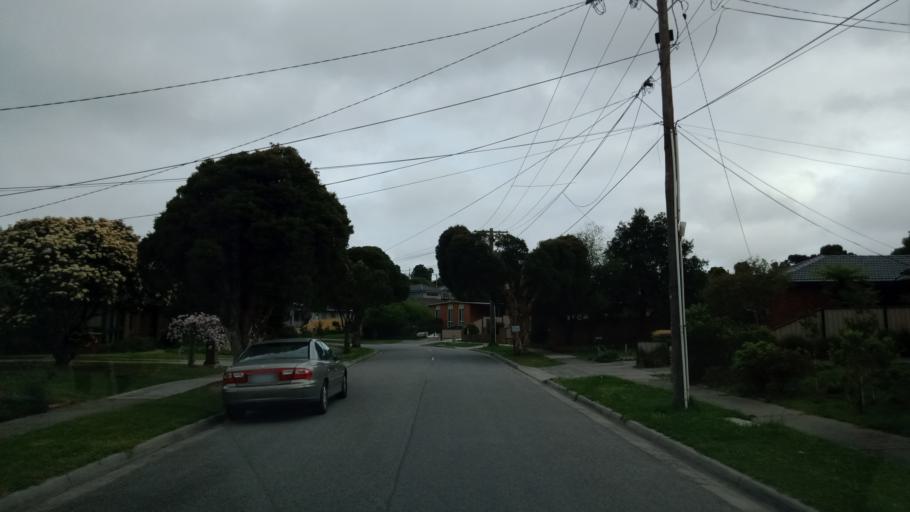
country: AU
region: Victoria
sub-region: Casey
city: Eumemmerring
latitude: -37.9907
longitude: 145.2510
